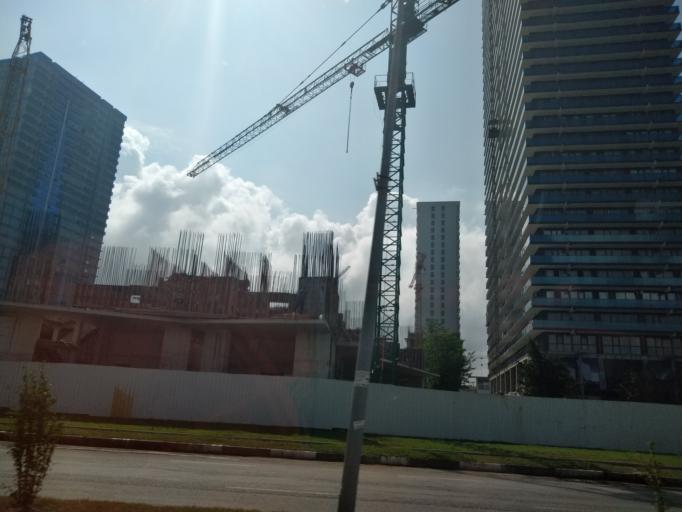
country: GE
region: Ajaria
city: Batumi
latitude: 41.6309
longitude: 41.6016
